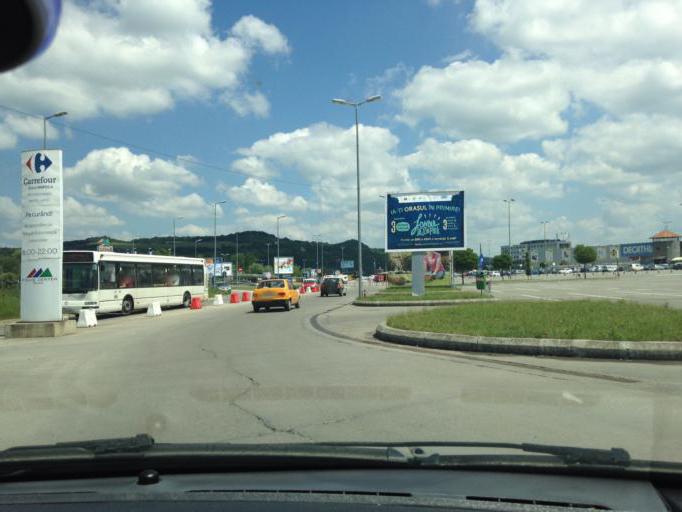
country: RO
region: Cluj
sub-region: Comuna Floresti
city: Floresti
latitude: 46.7511
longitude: 23.5306
